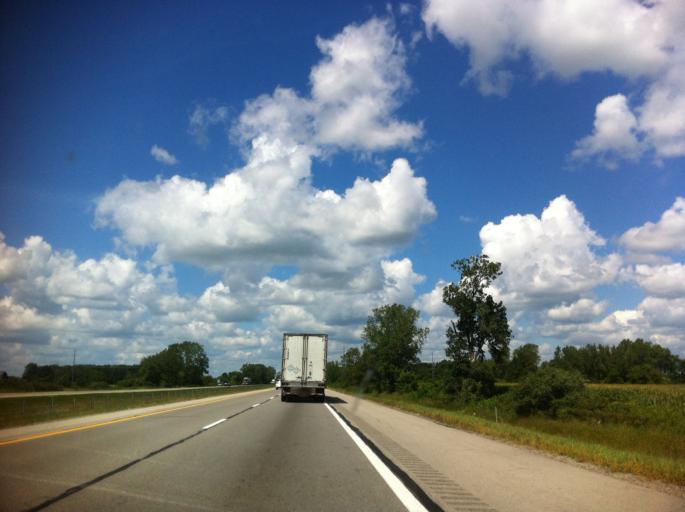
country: US
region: Michigan
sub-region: Monroe County
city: Dundee
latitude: 41.9938
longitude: -83.6785
